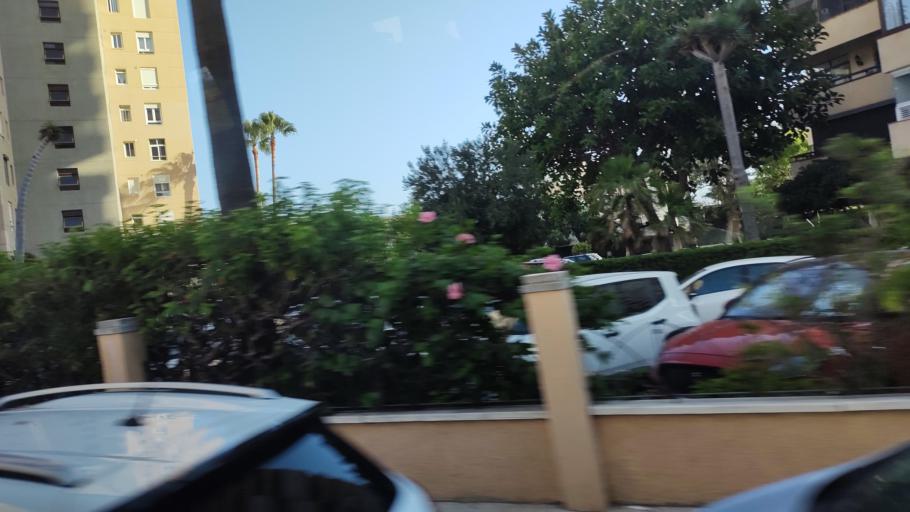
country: ES
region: Andalusia
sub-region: Provincia de Malaga
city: Torremolinos
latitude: 36.6300
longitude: -4.4909
